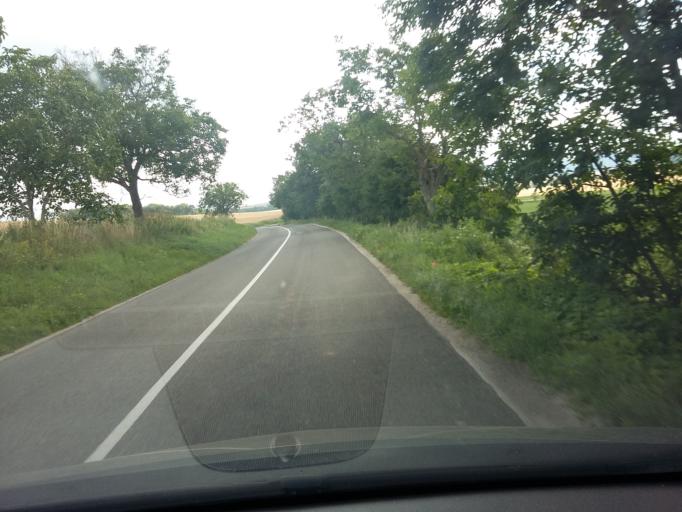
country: SK
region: Trnavsky
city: Smolenice
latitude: 48.5414
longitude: 17.3650
